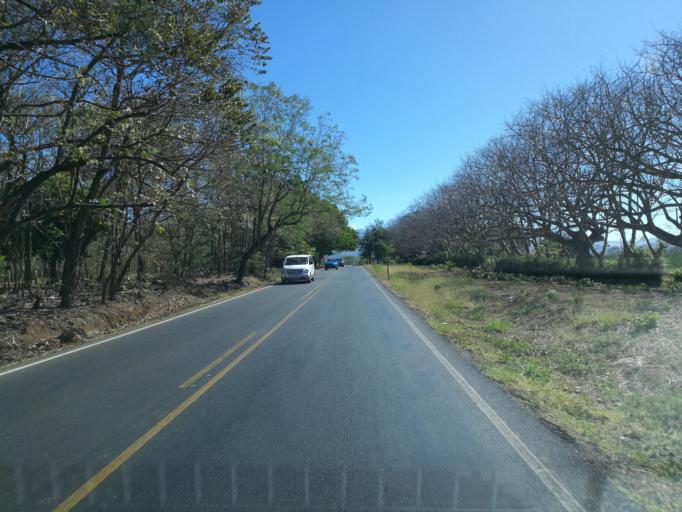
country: CR
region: Puntarenas
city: Miramar
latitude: 10.0930
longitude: -84.8230
